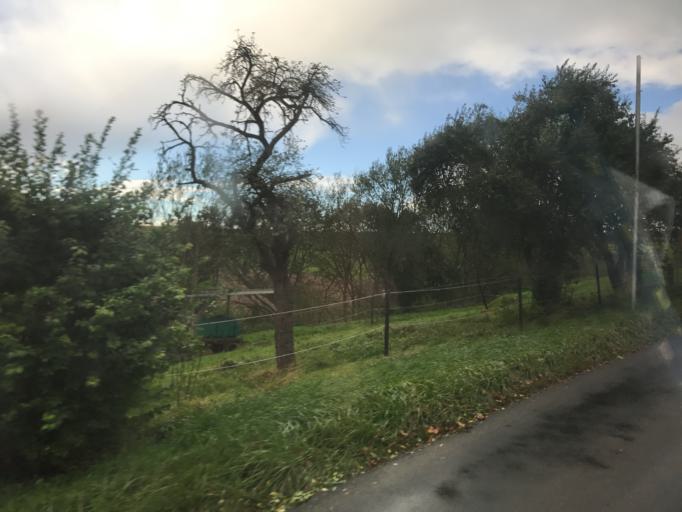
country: DE
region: Lower Saxony
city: Goettingen
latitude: 51.4898
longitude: 9.9814
